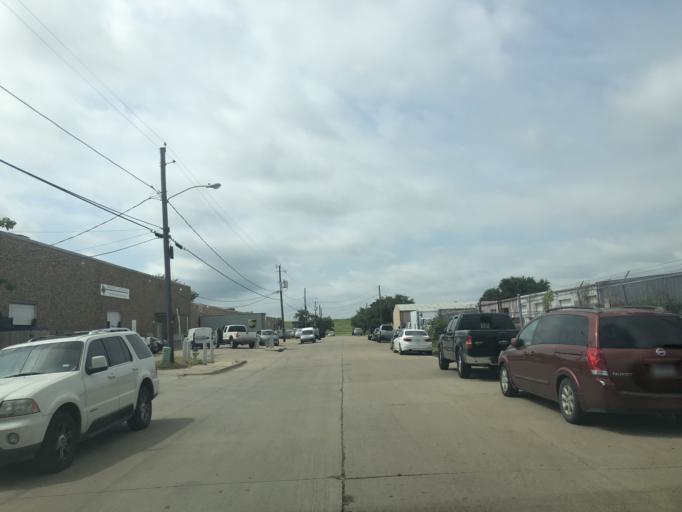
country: US
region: Texas
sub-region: Dallas County
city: Cockrell Hill
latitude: 32.8053
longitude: -96.8793
